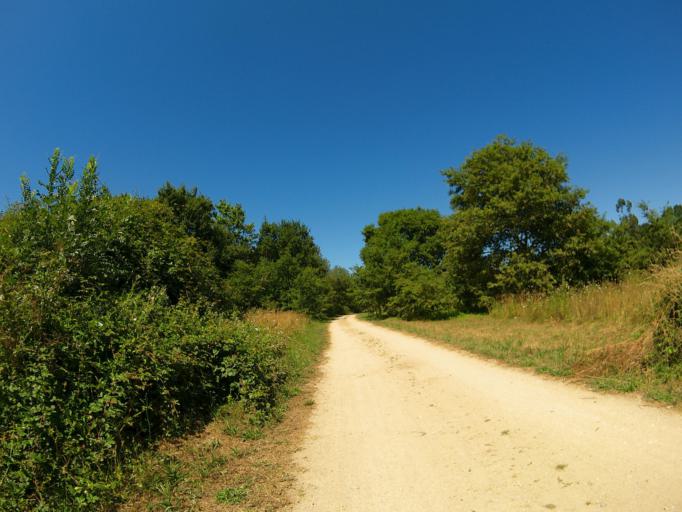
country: PT
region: Viana do Castelo
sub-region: Viana do Castelo
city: Darque
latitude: 41.7121
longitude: -8.7081
